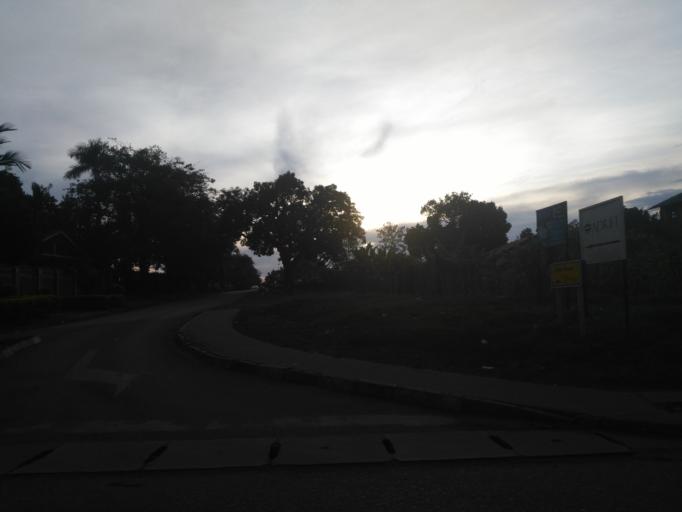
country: UG
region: Eastern Region
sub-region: Jinja District
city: Jinja
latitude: 0.4420
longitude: 33.1994
